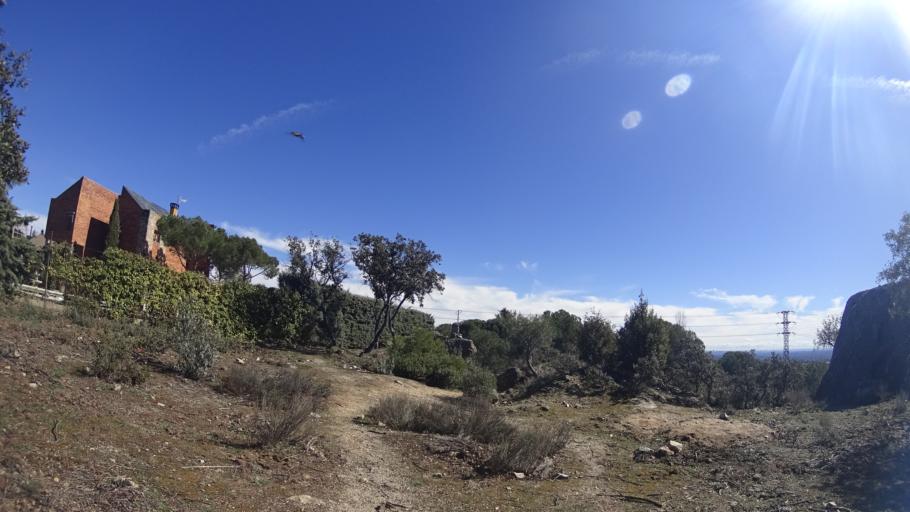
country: ES
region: Madrid
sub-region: Provincia de Madrid
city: Torrelodones
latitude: 40.5811
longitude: -3.9211
